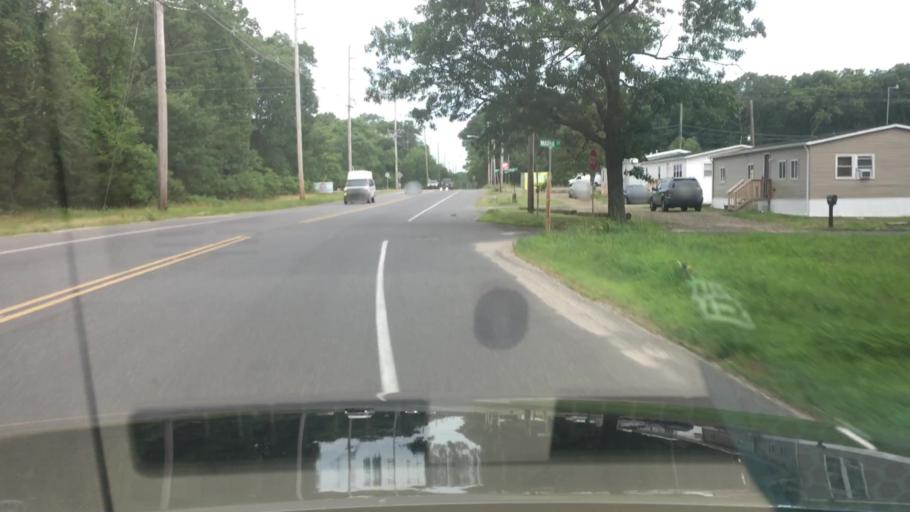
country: US
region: New Jersey
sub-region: Ocean County
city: Cedar Glen West
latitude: 40.0445
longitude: -74.3212
